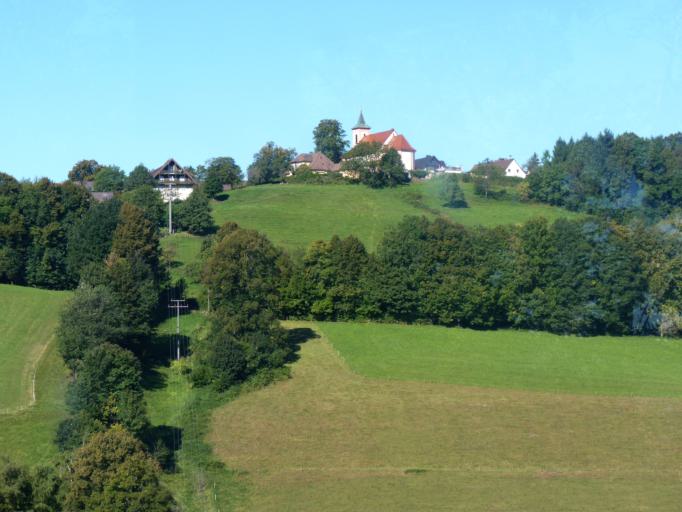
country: DE
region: Baden-Wuerttemberg
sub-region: Freiburg Region
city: Horben
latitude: 47.9334
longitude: 7.8679
